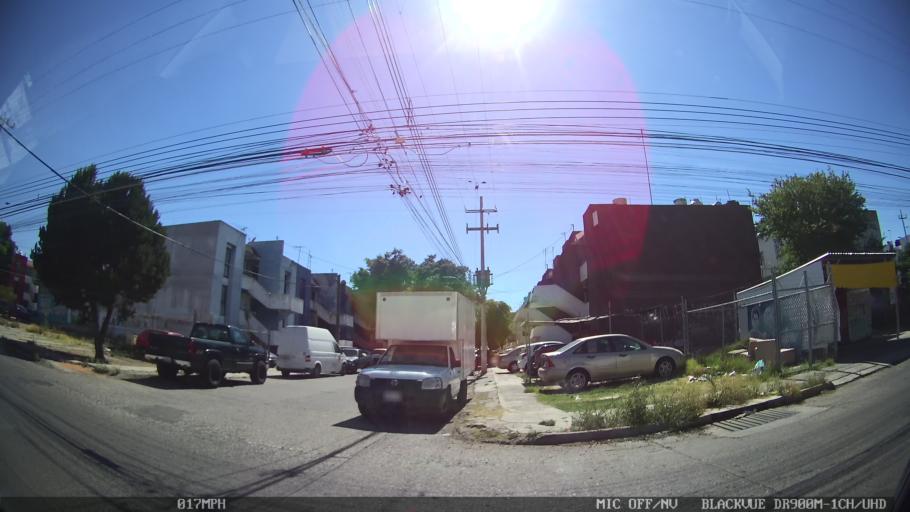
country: MX
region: Jalisco
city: Tlaquepaque
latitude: 20.6491
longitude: -103.2909
